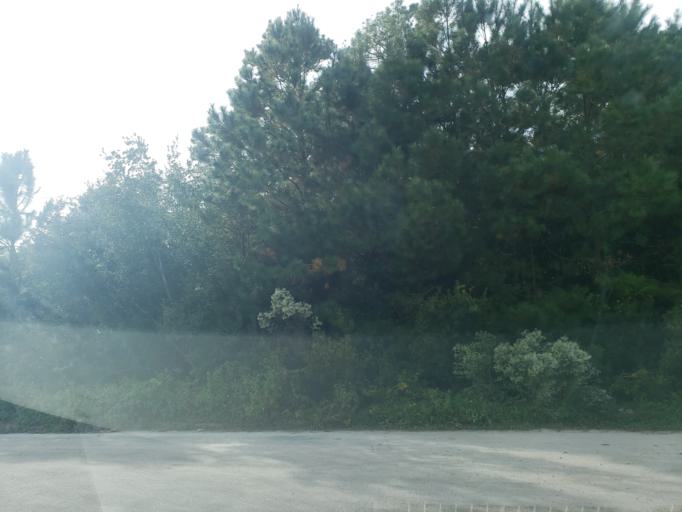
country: US
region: Georgia
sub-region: Chatham County
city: Georgetown
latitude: 32.0086
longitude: -81.2773
